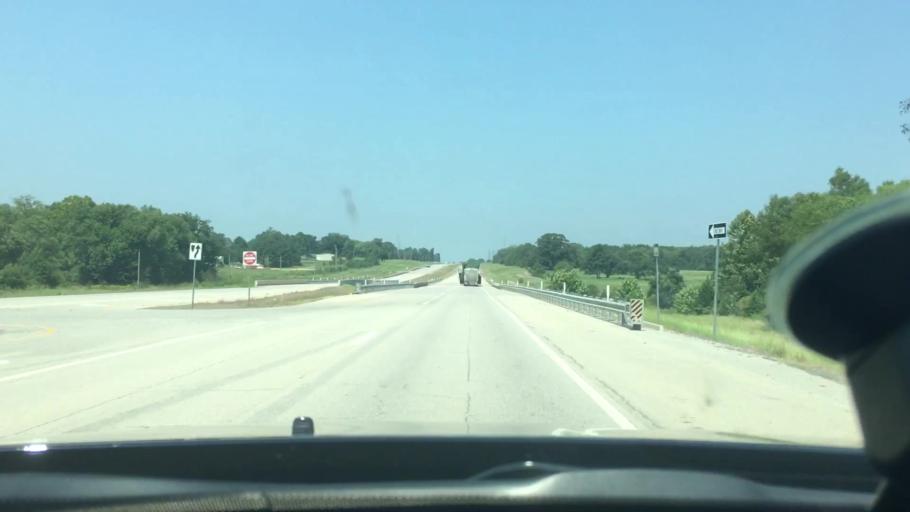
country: US
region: Oklahoma
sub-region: Atoka County
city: Atoka
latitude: 34.3231
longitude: -96.0398
